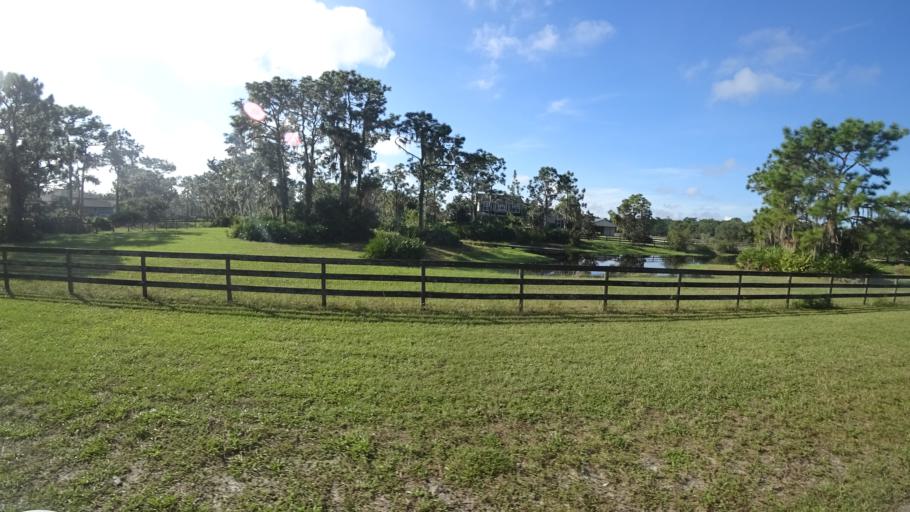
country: US
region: Florida
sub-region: Sarasota County
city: The Meadows
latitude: 27.4167
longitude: -82.3249
